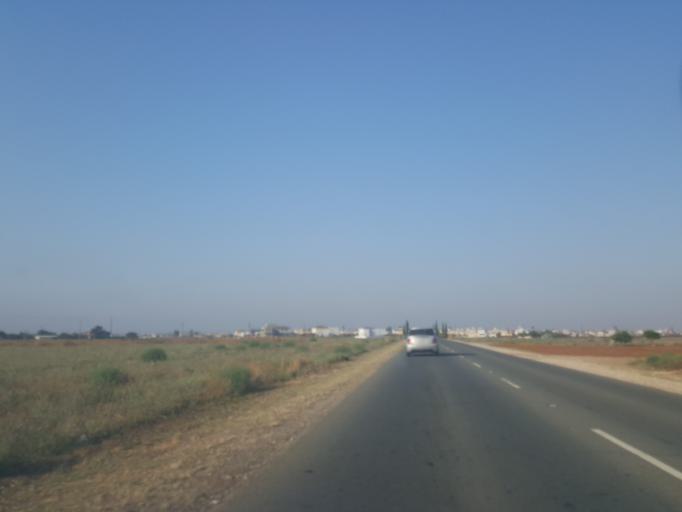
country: CY
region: Larnaka
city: Xylotymbou
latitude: 35.0290
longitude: 33.7548
